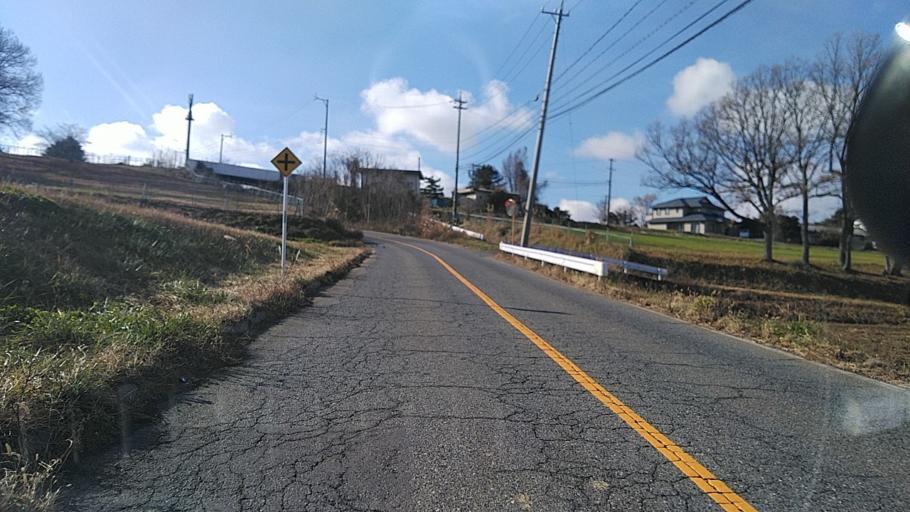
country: JP
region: Nagano
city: Shiojiri
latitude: 36.1246
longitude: 137.9806
